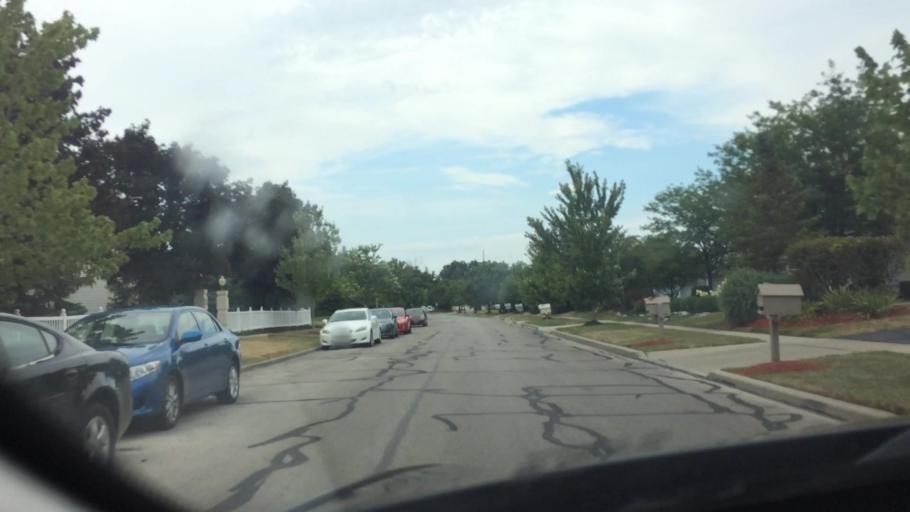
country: US
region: Ohio
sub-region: Lucas County
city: Ottawa Hills
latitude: 41.6502
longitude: -83.6571
